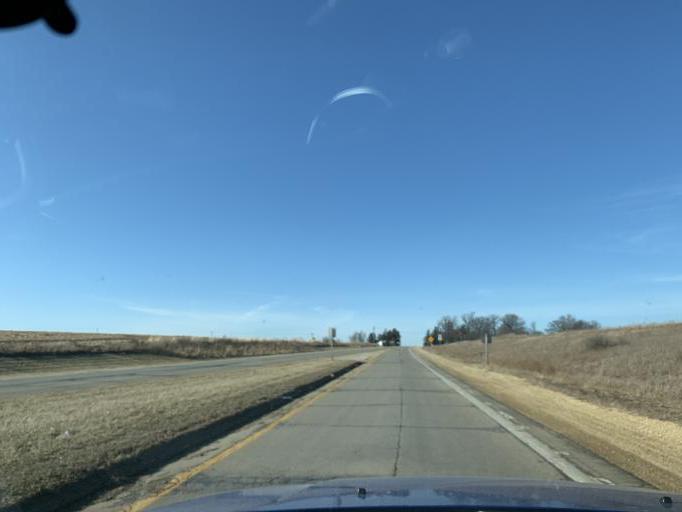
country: US
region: Wisconsin
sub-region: Green County
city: Monroe
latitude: 42.6193
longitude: -89.6568
